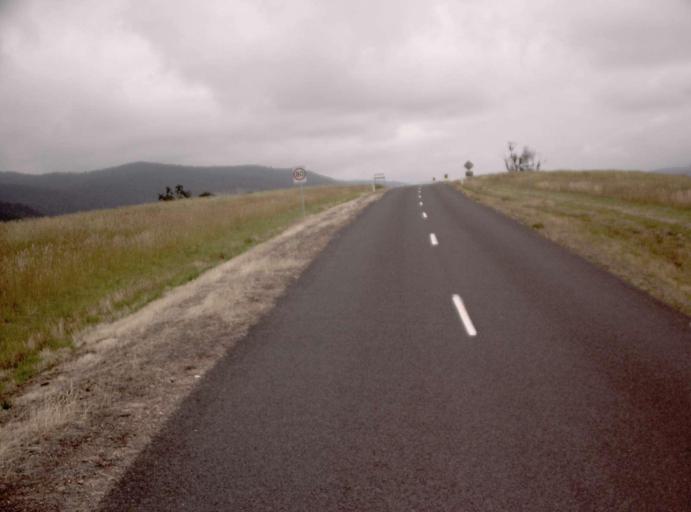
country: AU
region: Victoria
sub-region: Wellington
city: Heyfield
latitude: -37.8373
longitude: 146.6830
